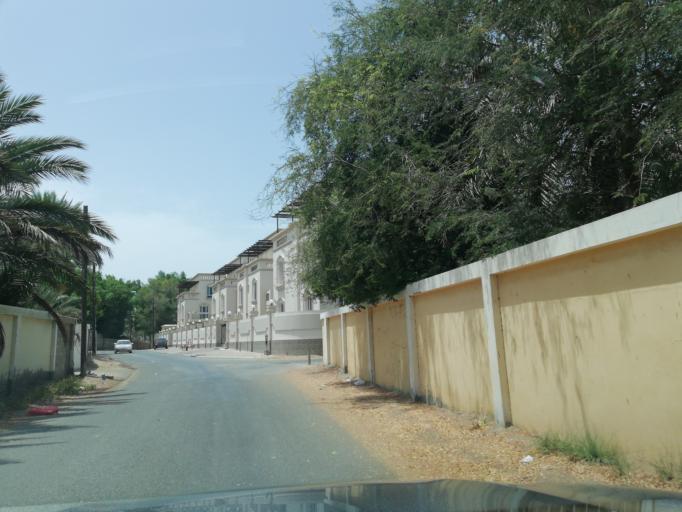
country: OM
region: Muhafazat Masqat
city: As Sib al Jadidah
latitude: 23.6591
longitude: 58.2117
